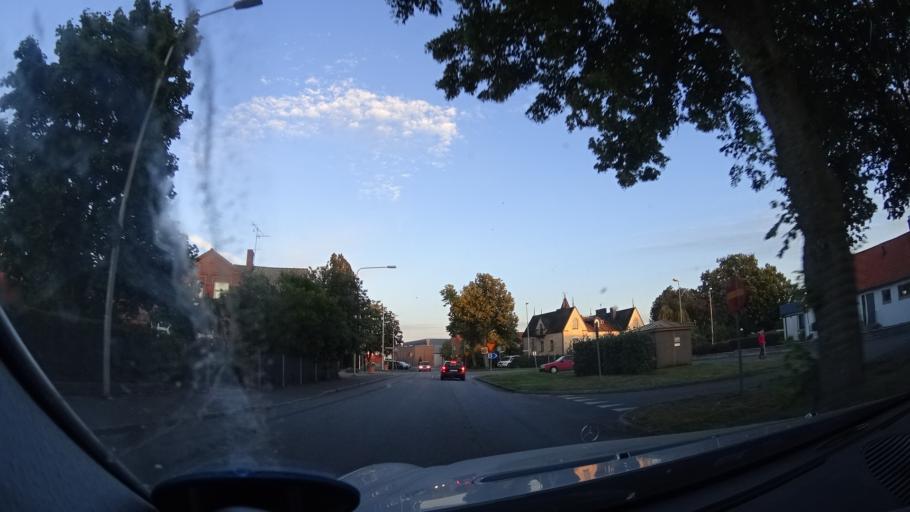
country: SE
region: Skane
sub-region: Kristianstads Kommun
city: Ahus
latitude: 55.9246
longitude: 14.2962
